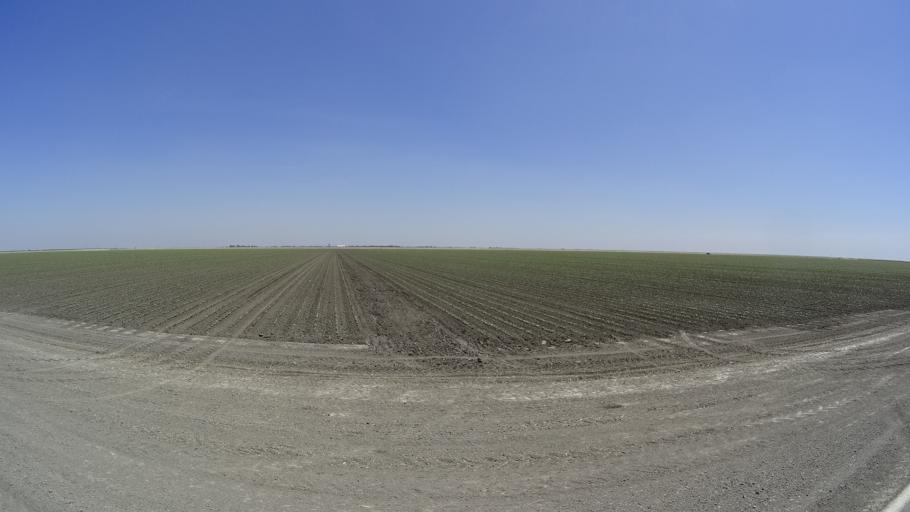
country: US
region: California
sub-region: Kings County
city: Corcoran
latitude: 36.0908
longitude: -119.6441
